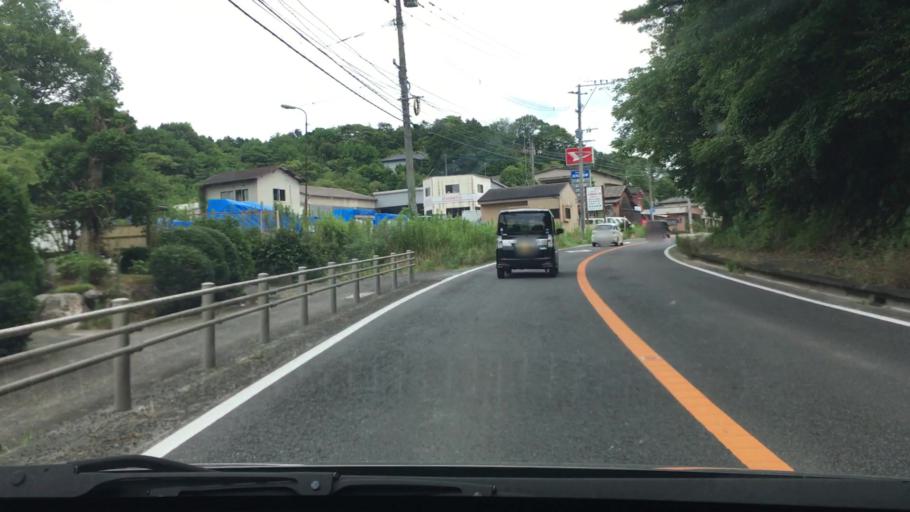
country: JP
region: Nagasaki
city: Togitsu
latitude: 32.9822
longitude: 129.7813
